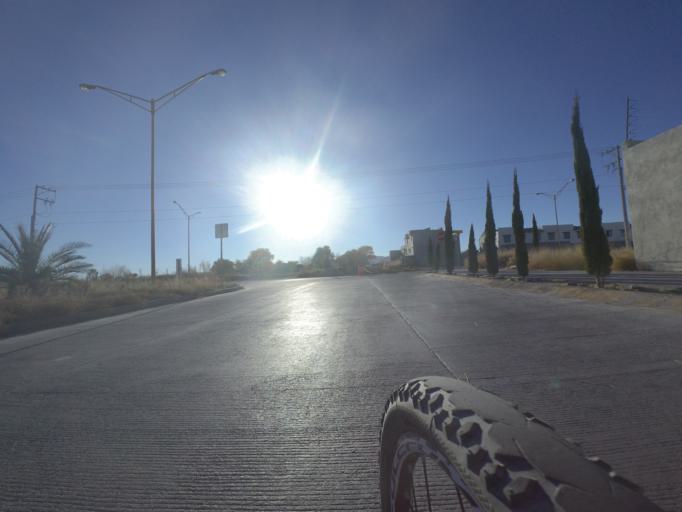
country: MX
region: Aguascalientes
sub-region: Aguascalientes
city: La Loma de los Negritos
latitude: 21.8525
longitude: -102.3457
